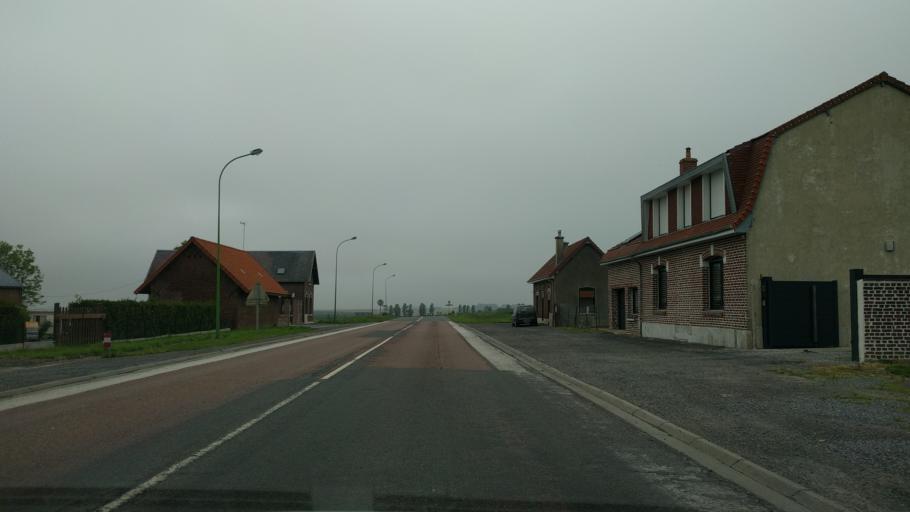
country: FR
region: Picardie
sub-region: Departement de la Somme
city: Moislains
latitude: 50.0340
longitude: 2.9137
